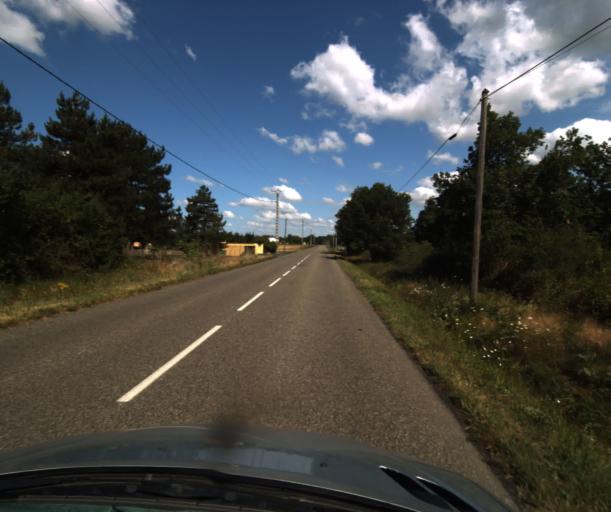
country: FR
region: Midi-Pyrenees
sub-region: Departement du Tarn-et-Garonne
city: Campsas
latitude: 43.9047
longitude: 1.2925
